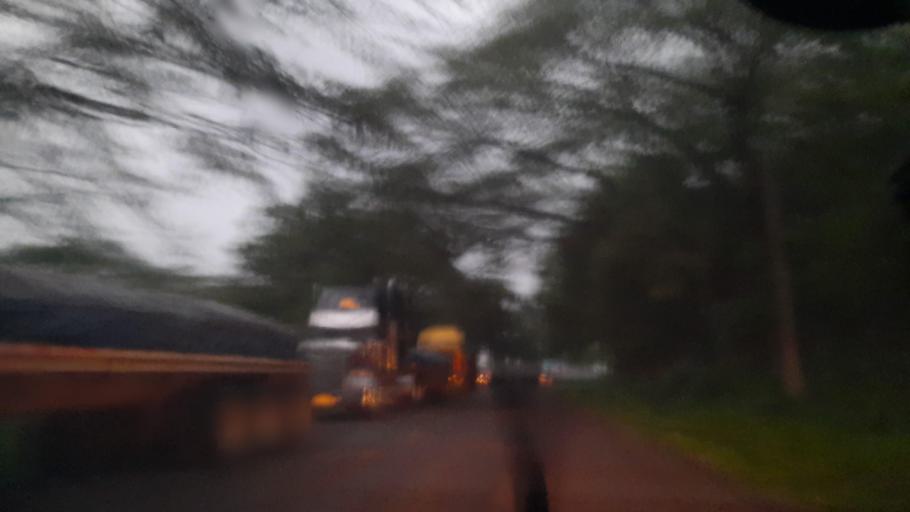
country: GT
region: Jutiapa
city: Atescatempa
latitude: 14.2152
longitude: -89.6874
